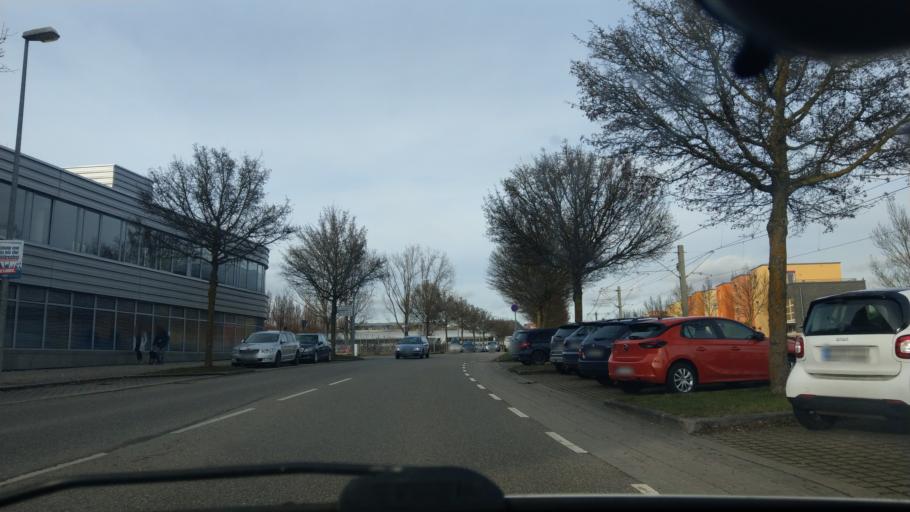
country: DE
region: Baden-Wuerttemberg
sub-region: Regierungsbezirk Stuttgart
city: Ostfildern
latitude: 48.7156
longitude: 9.2725
